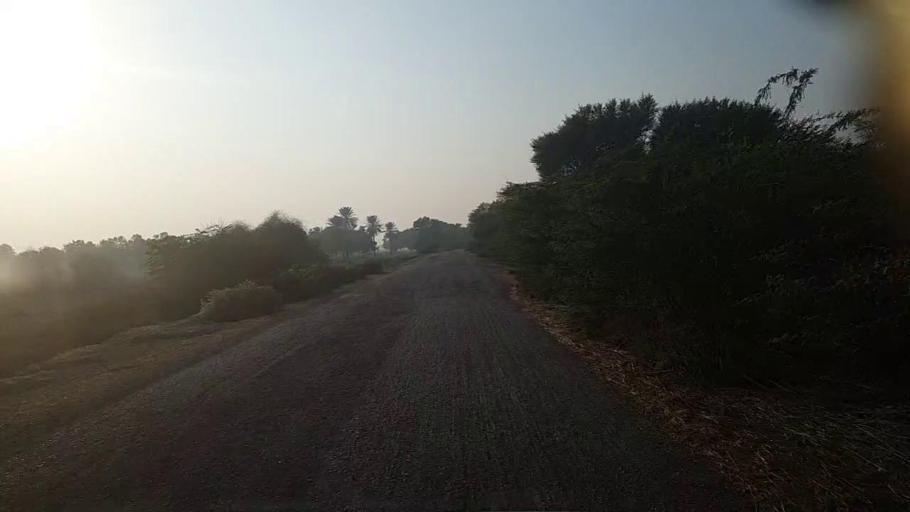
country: PK
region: Sindh
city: Pad Idan
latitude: 26.7183
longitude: 68.4186
